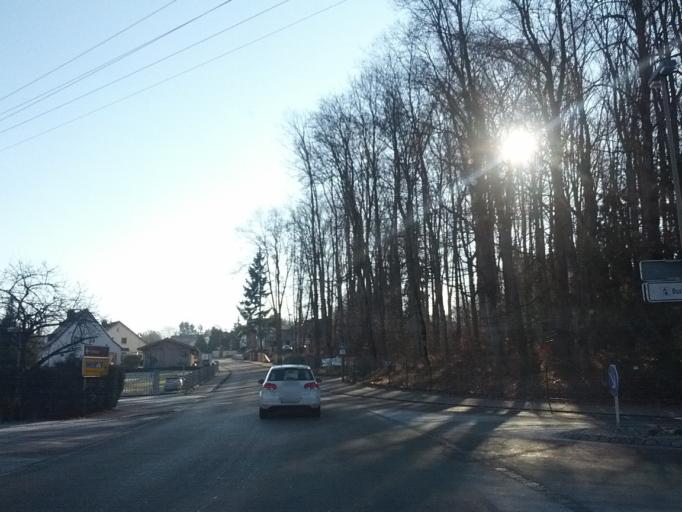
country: DE
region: Bavaria
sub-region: Swabia
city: Buxheim
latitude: 47.9958
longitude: 10.1355
